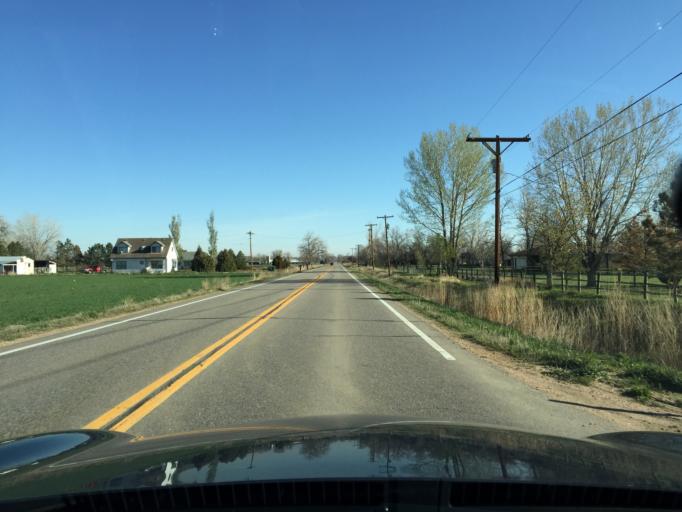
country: US
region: Colorado
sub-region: Boulder County
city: Erie
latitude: 40.0755
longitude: -105.0554
